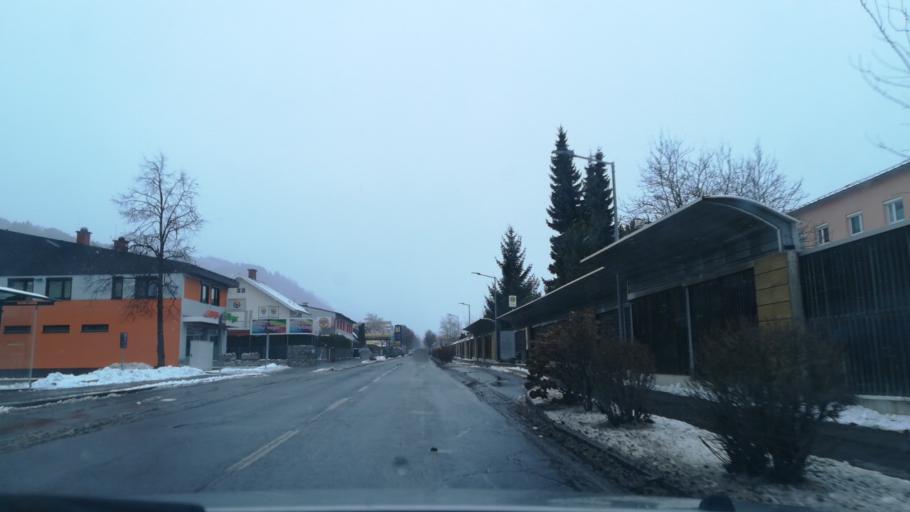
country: AT
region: Styria
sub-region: Politischer Bezirk Murtal
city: Judenburg
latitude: 47.1694
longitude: 14.6492
